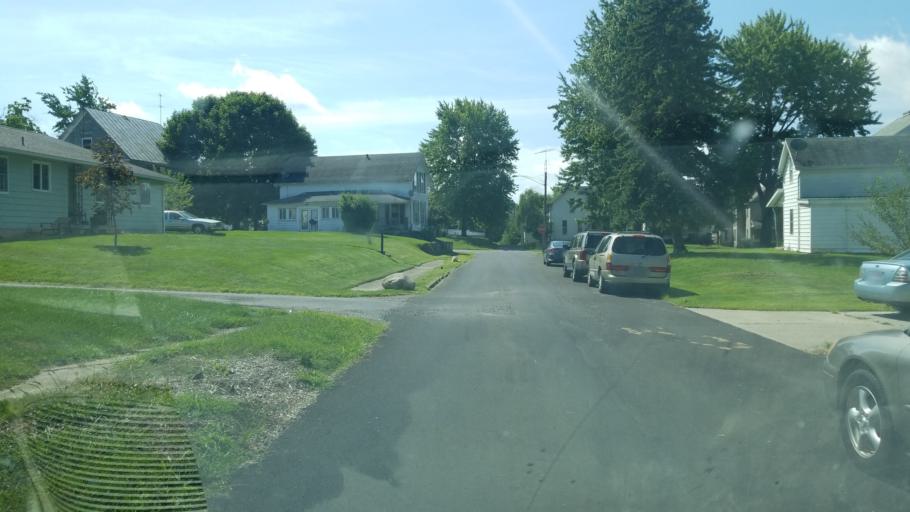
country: US
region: Ohio
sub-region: Hardin County
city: Kenton
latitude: 40.6471
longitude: -83.6002
